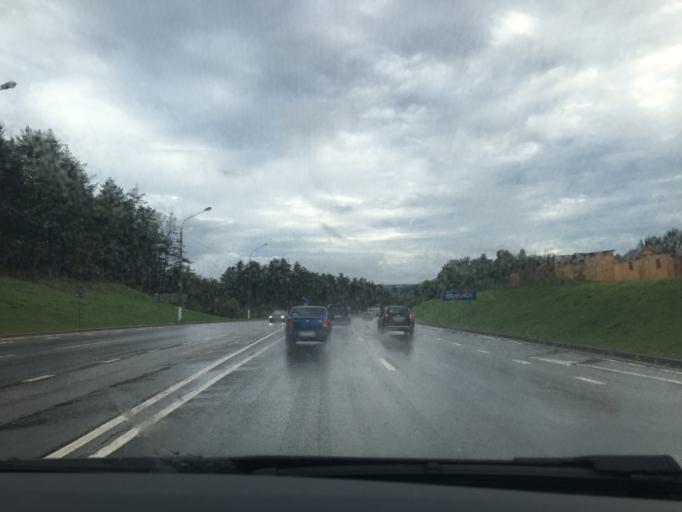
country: RU
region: Kaluga
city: Obninsk
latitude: 55.0563
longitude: 36.6184
